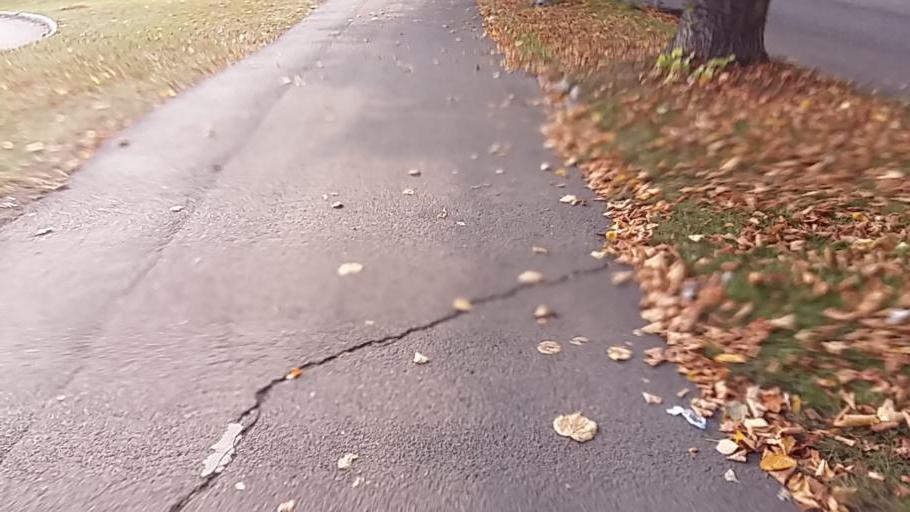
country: SE
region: Joenkoeping
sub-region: Jonkopings Kommun
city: Jonkoping
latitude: 57.7725
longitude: 14.1565
